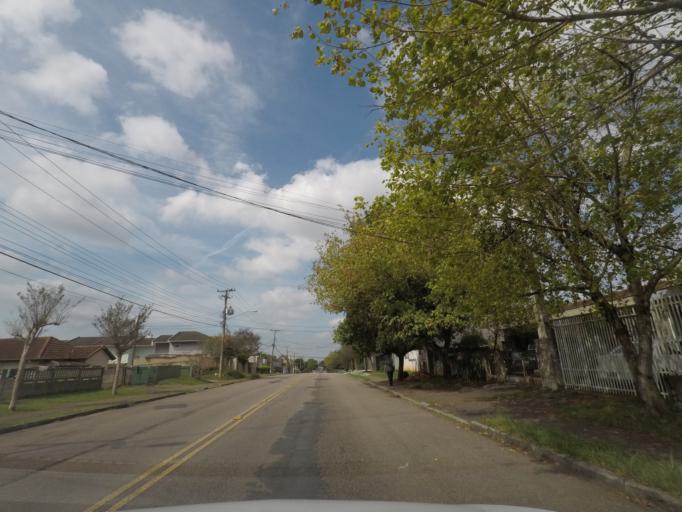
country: BR
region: Parana
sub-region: Pinhais
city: Pinhais
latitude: -25.4440
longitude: -49.2274
